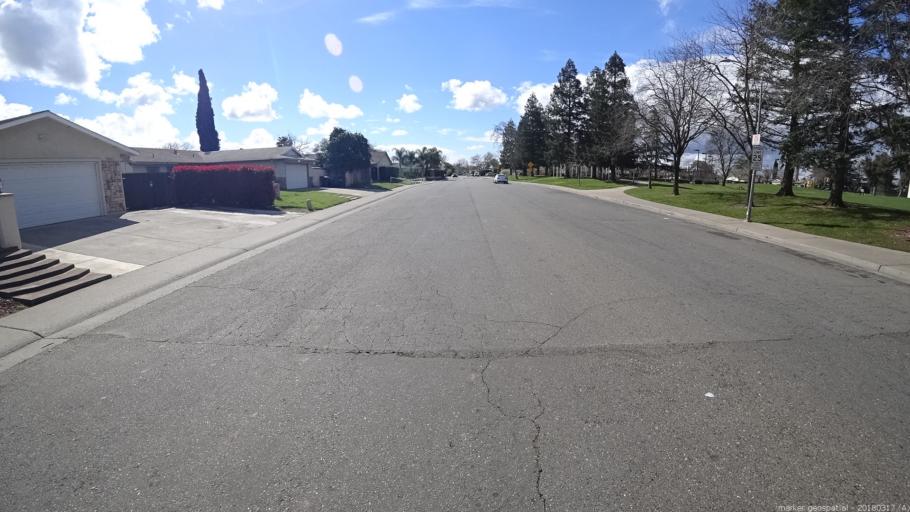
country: US
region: California
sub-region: Sacramento County
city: Florin
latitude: 38.4740
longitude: -121.3972
